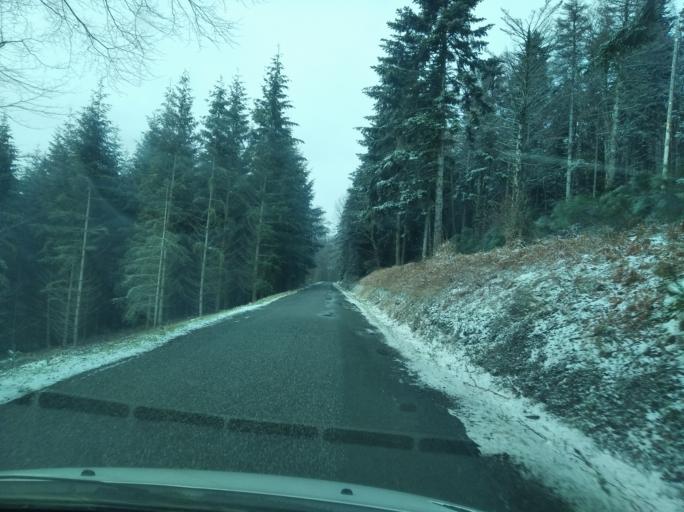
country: FR
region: Rhone-Alpes
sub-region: Departement de la Loire
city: La Pacaudiere
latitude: 46.1239
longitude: 3.7960
